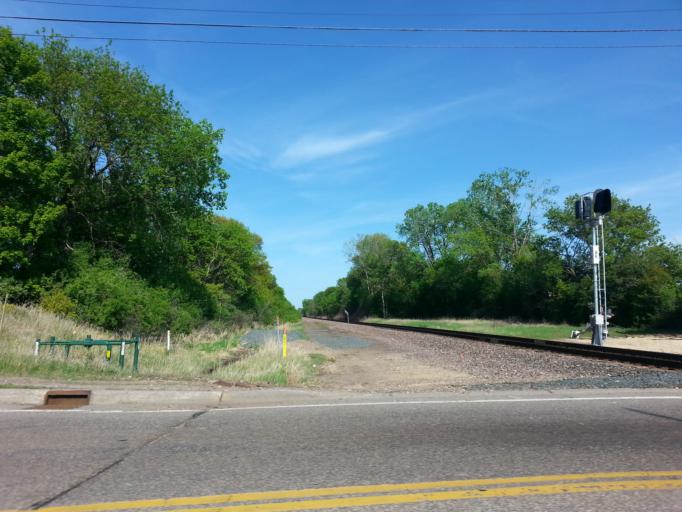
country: US
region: Minnesota
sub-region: Washington County
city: Oakdale
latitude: 44.9945
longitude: -92.9442
